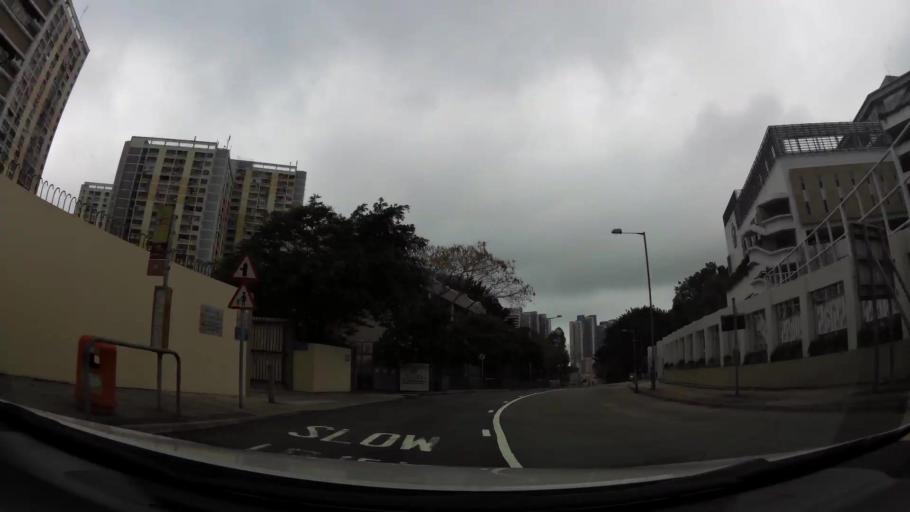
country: HK
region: Central and Western
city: Central
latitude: 22.2534
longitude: 114.1385
